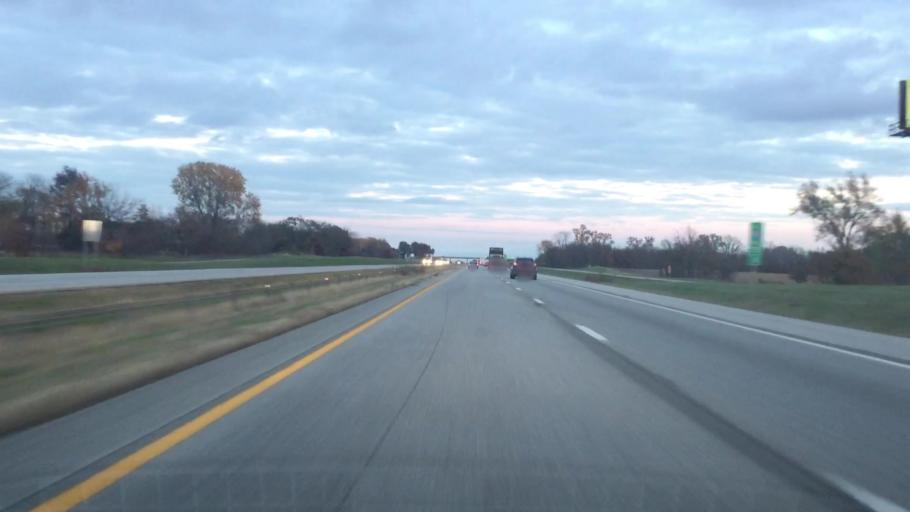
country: US
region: Missouri
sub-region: Saline County
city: Sweet Springs
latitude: 38.9736
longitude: -93.3427
